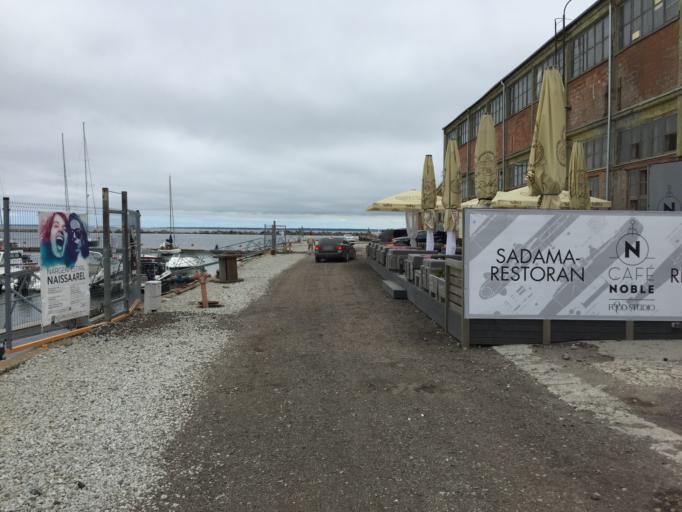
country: EE
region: Harju
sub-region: Tallinna linn
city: Tallinn
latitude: 59.4523
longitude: 24.7301
